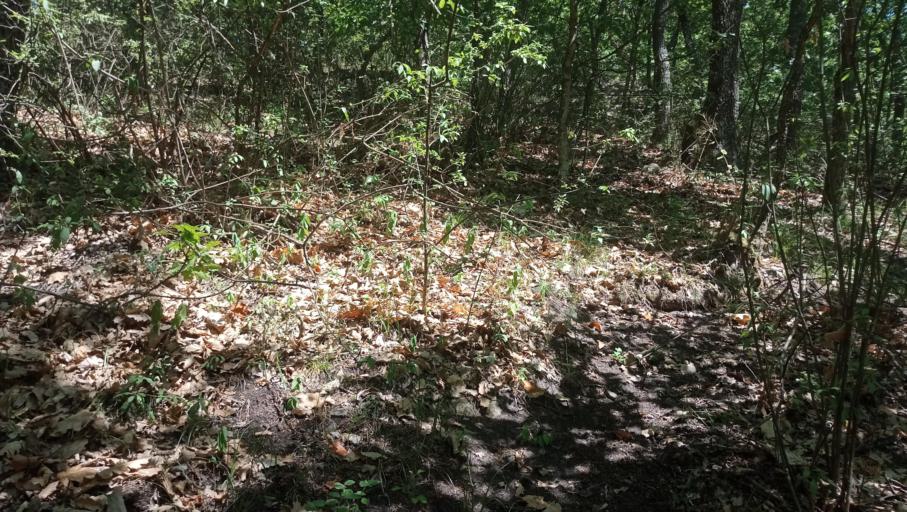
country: HU
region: Nograd
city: Matraverebely
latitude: 48.0094
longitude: 19.7622
